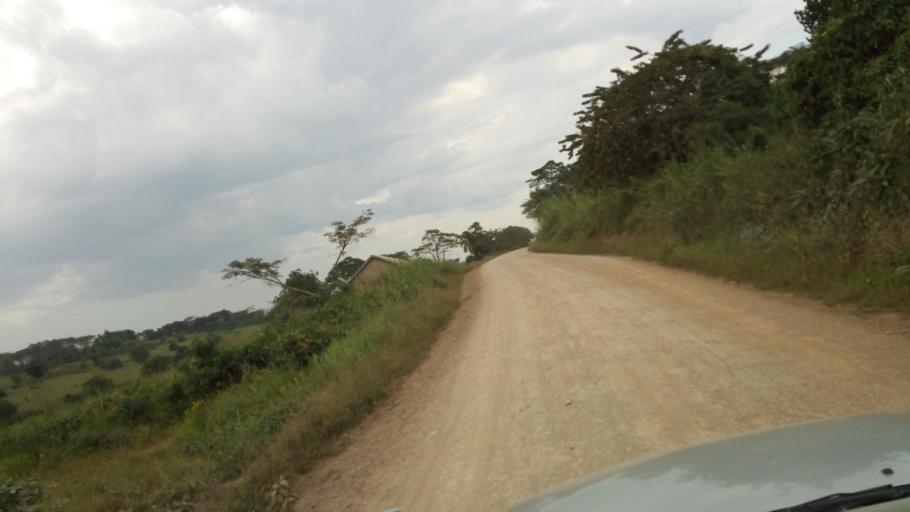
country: UG
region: Central Region
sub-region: Kiboga District
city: Kiboga
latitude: 0.7163
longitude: 31.7464
